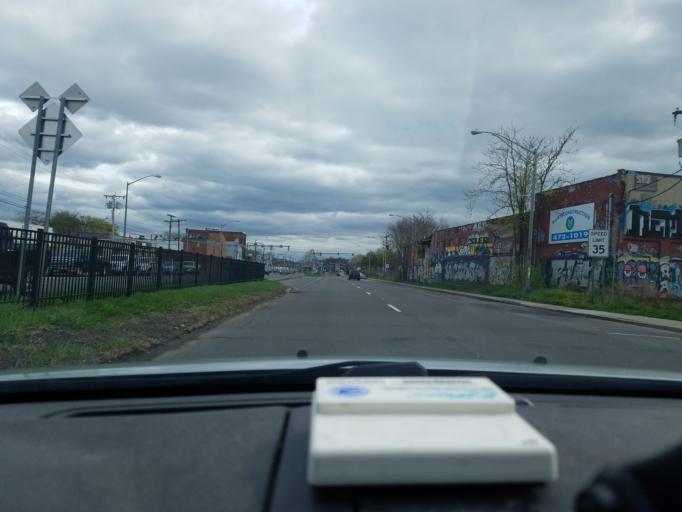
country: US
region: New York
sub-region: Onondaga County
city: Syracuse
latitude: 43.0459
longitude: -76.1587
